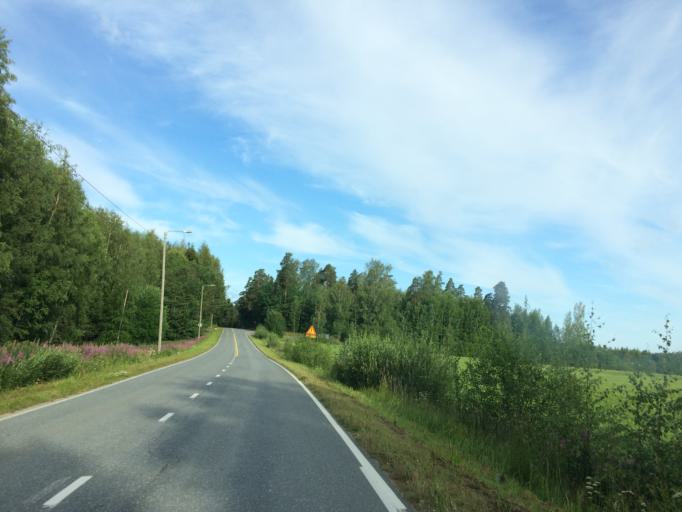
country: FI
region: Haeme
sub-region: Haemeenlinna
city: Janakkala
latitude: 60.9285
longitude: 24.5802
